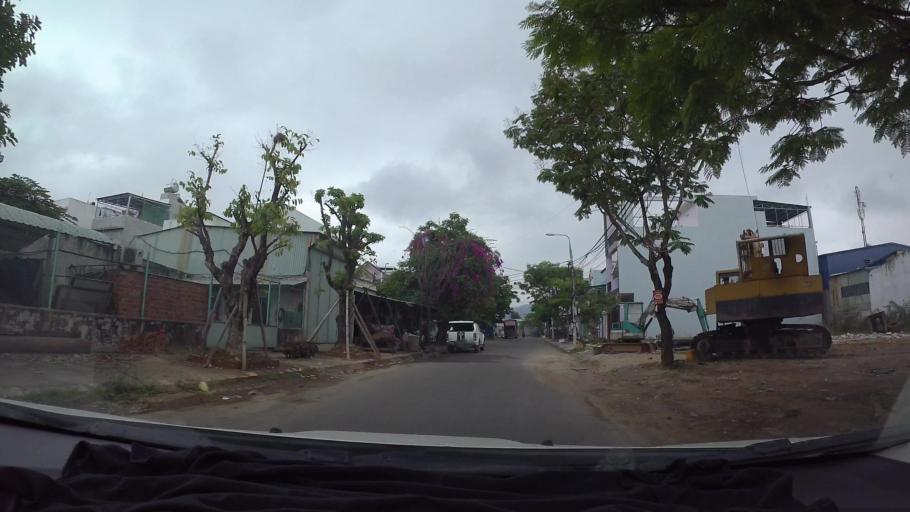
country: VN
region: Da Nang
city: Lien Chieu
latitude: 16.0534
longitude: 108.1592
